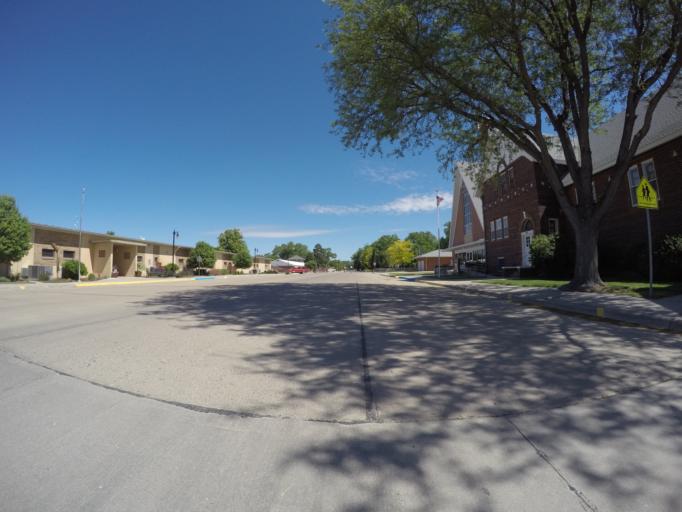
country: US
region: Kansas
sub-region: Rawlins County
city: Atwood
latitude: 39.8087
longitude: -101.0422
